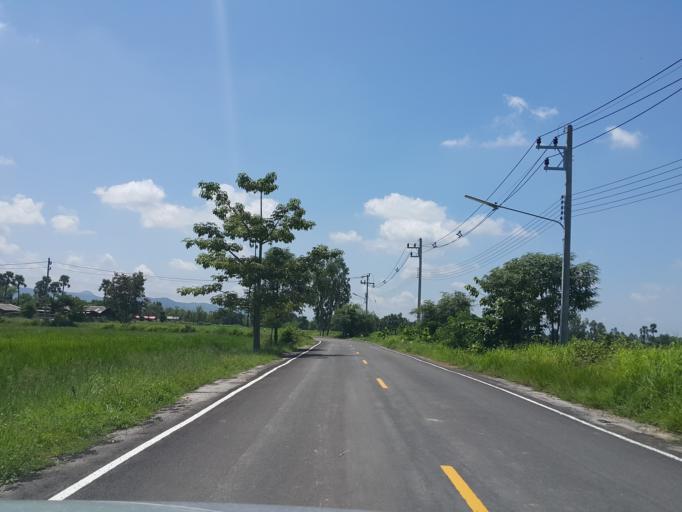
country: TH
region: Lamphun
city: Ban Thi
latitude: 18.6764
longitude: 99.1295
